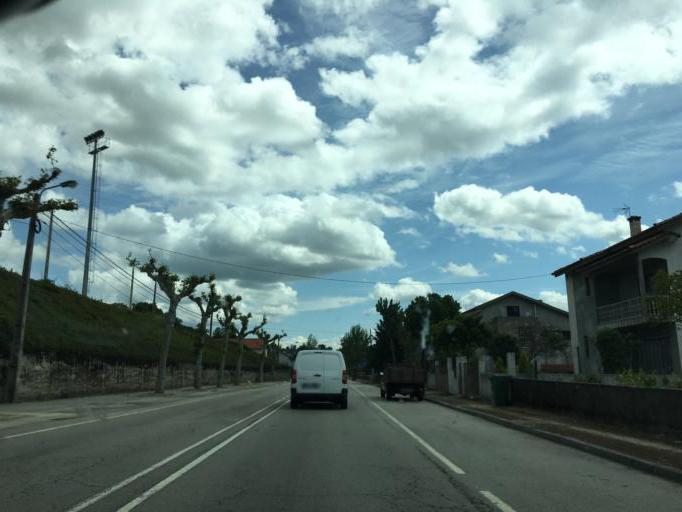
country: PT
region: Vila Real
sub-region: Boticas
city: Boticas
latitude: 41.6915
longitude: -7.6574
